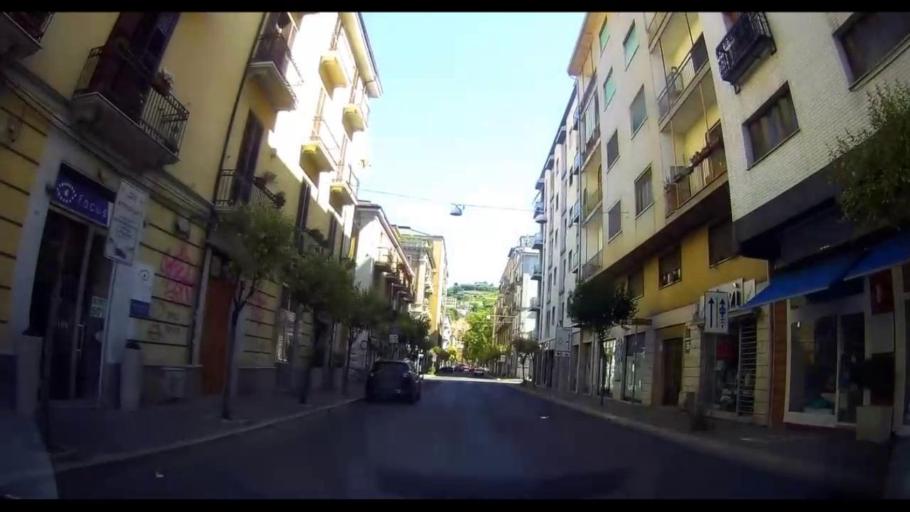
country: IT
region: Calabria
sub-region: Provincia di Cosenza
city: Cosenza
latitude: 39.2960
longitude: 16.2536
